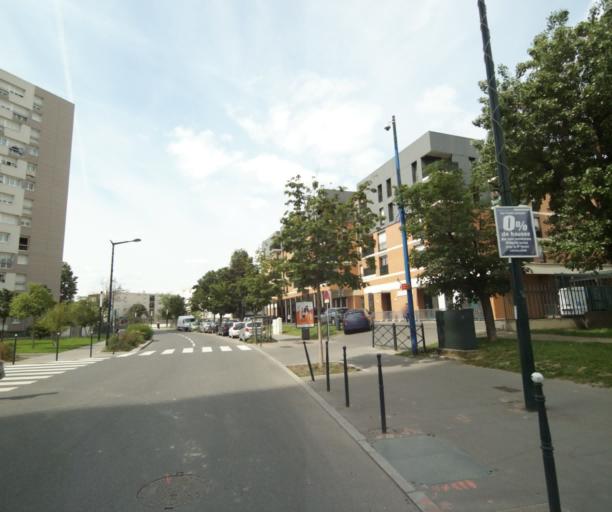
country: FR
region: Ile-de-France
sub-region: Departement des Hauts-de-Seine
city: Bois-Colombes
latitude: 48.9316
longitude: 2.2806
